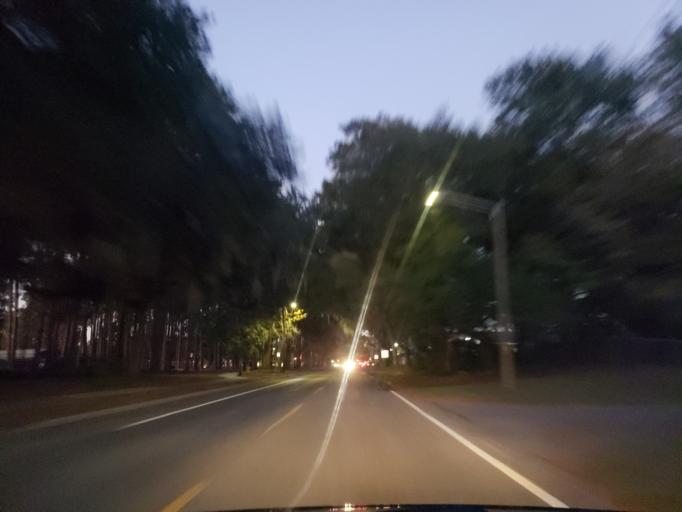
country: US
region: Georgia
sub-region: Chatham County
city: Thunderbolt
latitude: 32.0434
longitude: -81.0775
